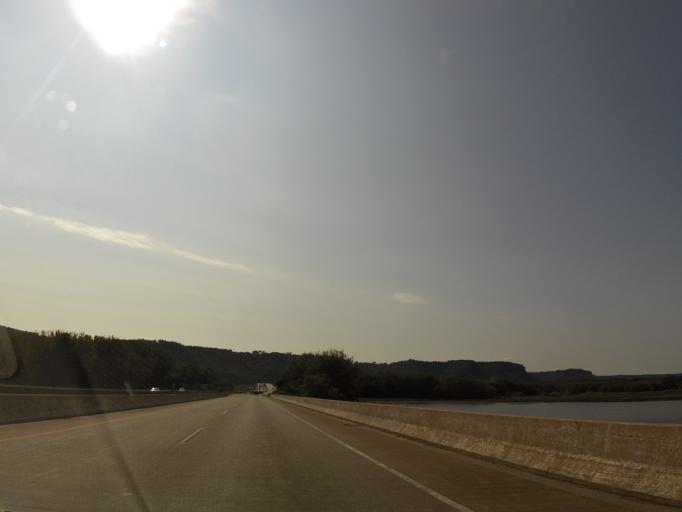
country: US
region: Wisconsin
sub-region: La Crosse County
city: French Island
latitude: 43.8594
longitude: -91.2830
